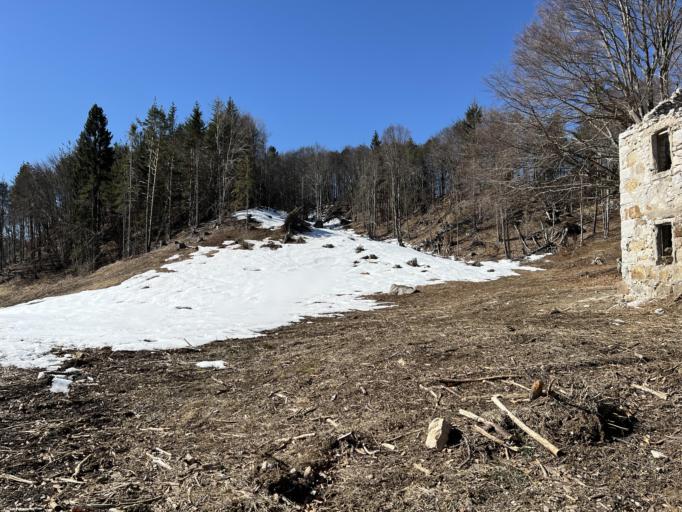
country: IT
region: Friuli Venezia Giulia
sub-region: Provincia di Udine
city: Zuglio
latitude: 46.4487
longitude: 13.0773
